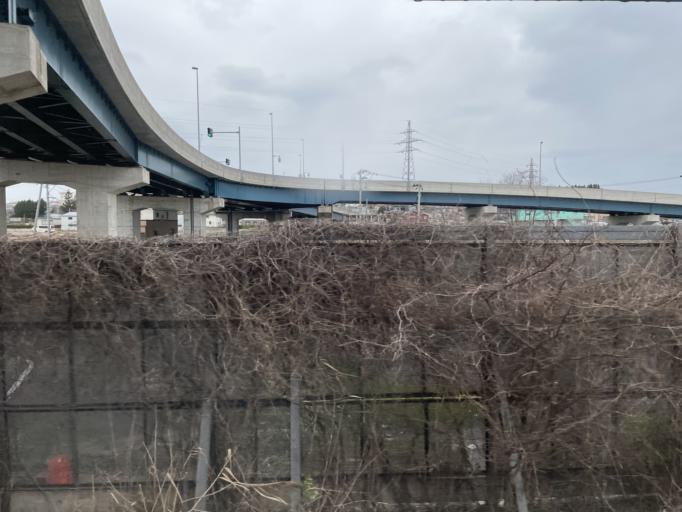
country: JP
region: Aomori
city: Namioka
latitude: 40.7076
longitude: 140.5781
